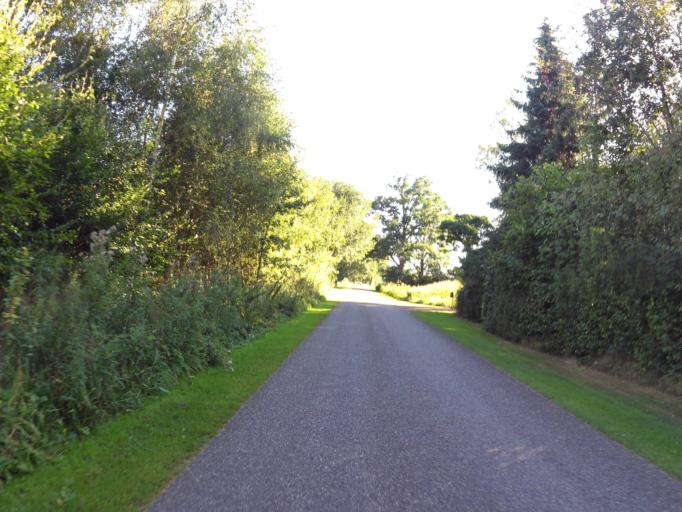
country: NL
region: Gelderland
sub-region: Gemeente Winterswijk
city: Winterswijk
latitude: 51.9278
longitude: 6.7575
